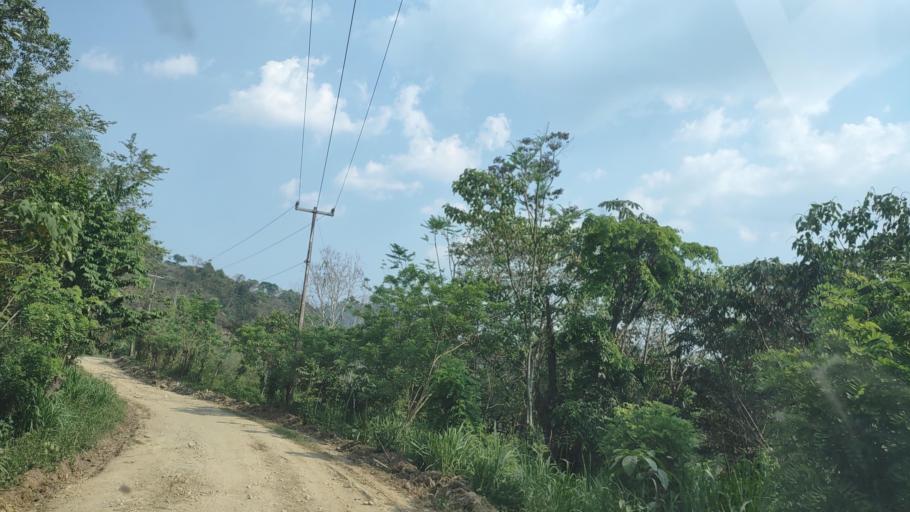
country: MX
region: Chiapas
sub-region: Tecpatan
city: Raudales Malpaso
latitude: 17.3217
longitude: -93.7431
